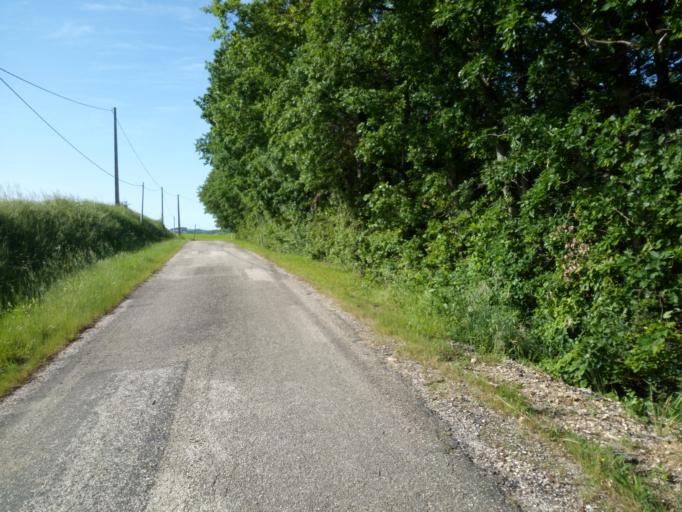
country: FR
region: Midi-Pyrenees
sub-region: Departement du Tarn-et-Garonne
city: Molieres
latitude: 44.1815
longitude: 1.2917
